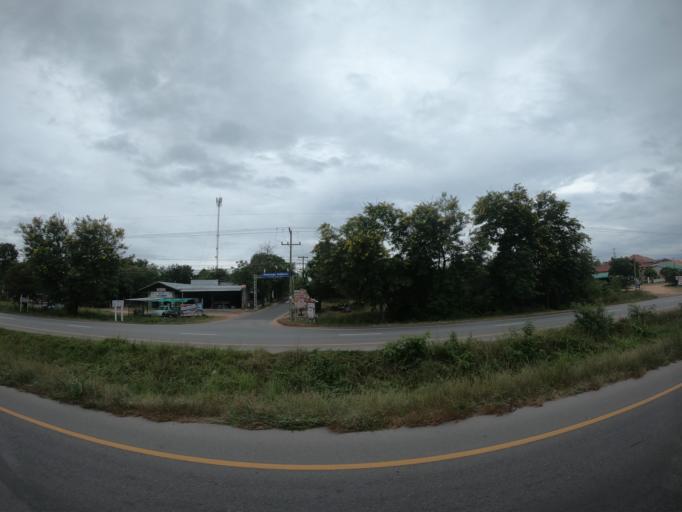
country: TH
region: Roi Et
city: Changhan
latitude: 16.1100
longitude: 103.5072
